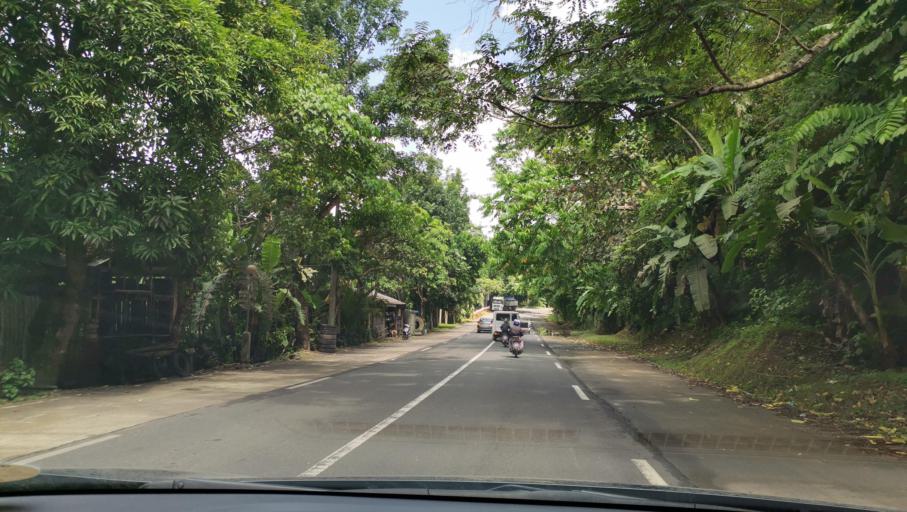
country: PH
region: Calabarzon
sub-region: Province of Quezon
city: Rizal
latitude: 13.9477
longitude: 122.2889
